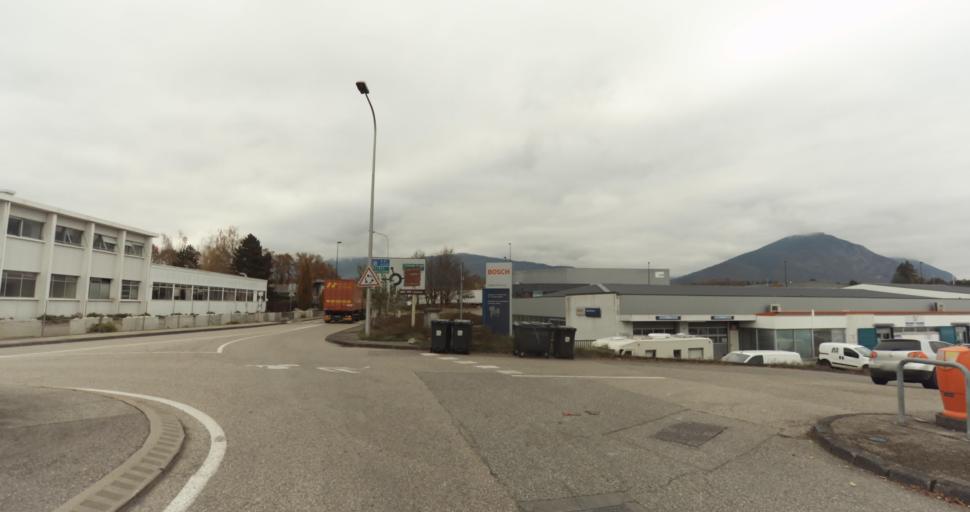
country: FR
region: Rhone-Alpes
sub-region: Departement de la Haute-Savoie
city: Pringy
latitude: 45.9382
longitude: 6.1253
